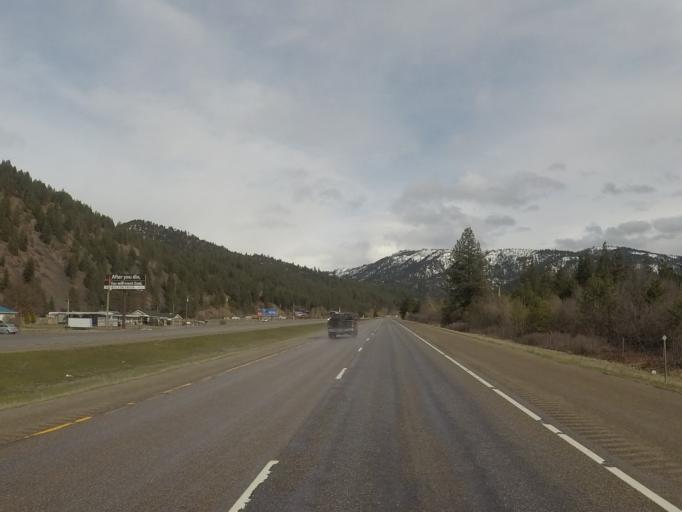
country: US
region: Montana
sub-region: Missoula County
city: Clinton
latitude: 46.7901
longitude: -113.7313
